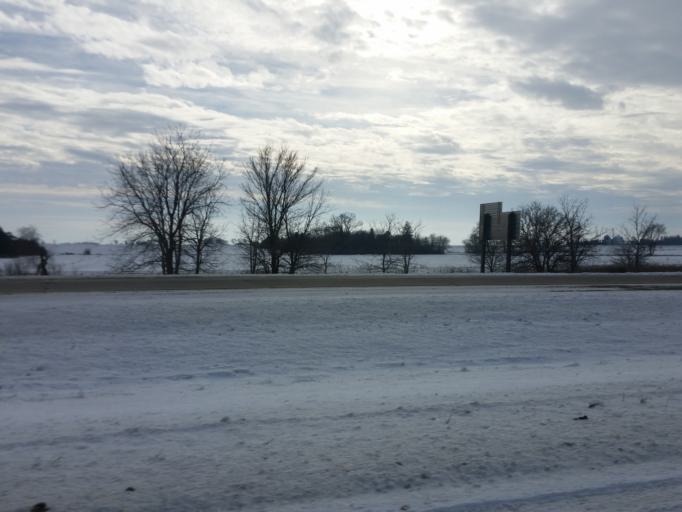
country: US
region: Iowa
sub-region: Buchanan County
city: Independence
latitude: 42.4478
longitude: -91.9264
